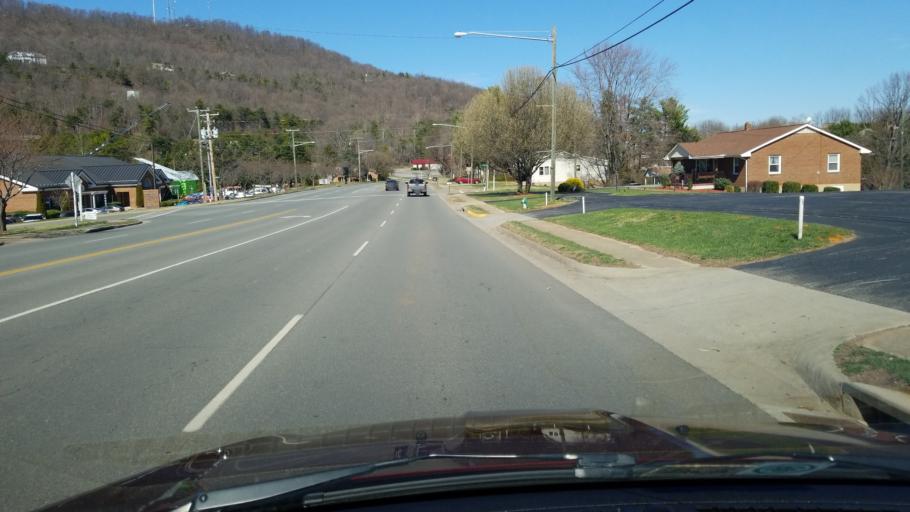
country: US
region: Virginia
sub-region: Franklin County
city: Rocky Mount
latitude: 37.0142
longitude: -79.8925
